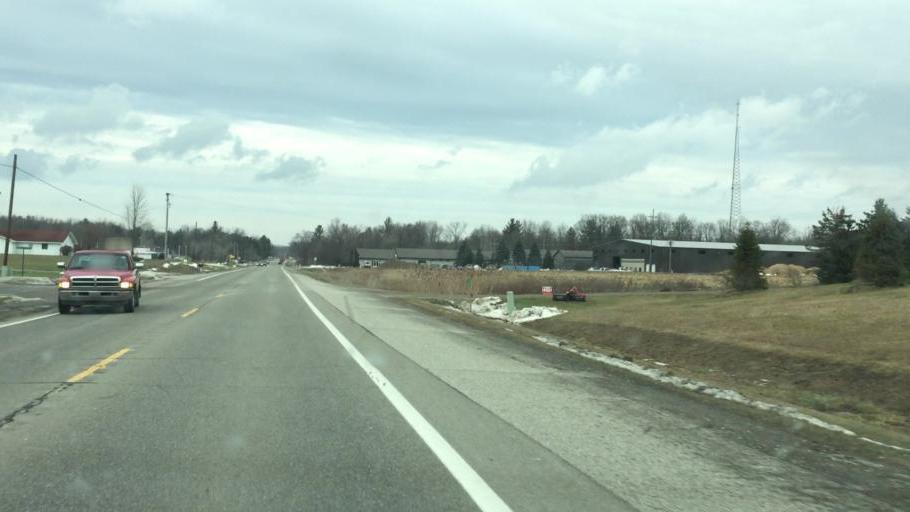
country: US
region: Michigan
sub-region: Lapeer County
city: Barnes Lake-Millers Lake
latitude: 43.1938
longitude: -83.3127
